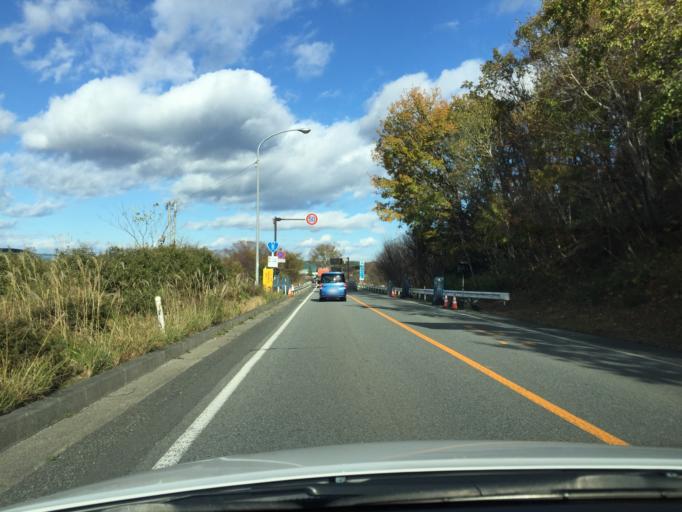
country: JP
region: Fukushima
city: Namie
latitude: 37.4781
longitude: 141.0074
